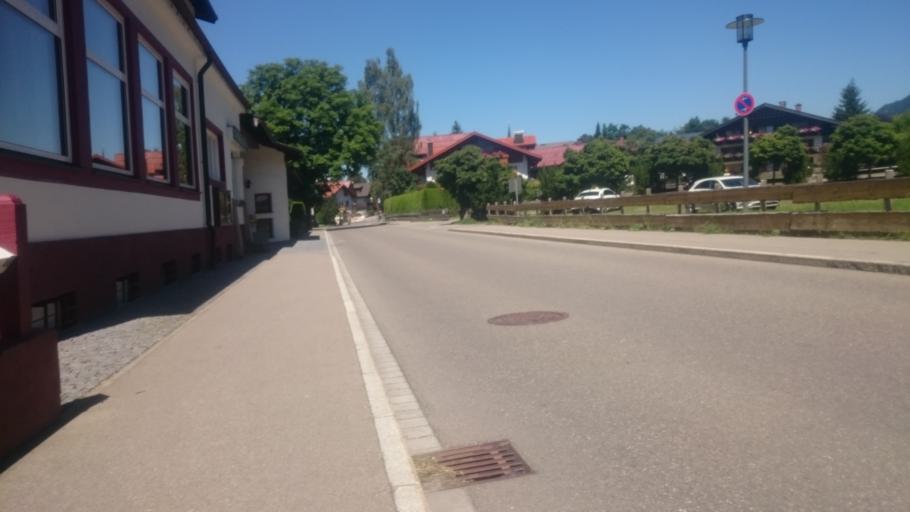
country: DE
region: Bavaria
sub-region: Swabia
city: Oberstdorf
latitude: 47.4022
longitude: 10.2787
